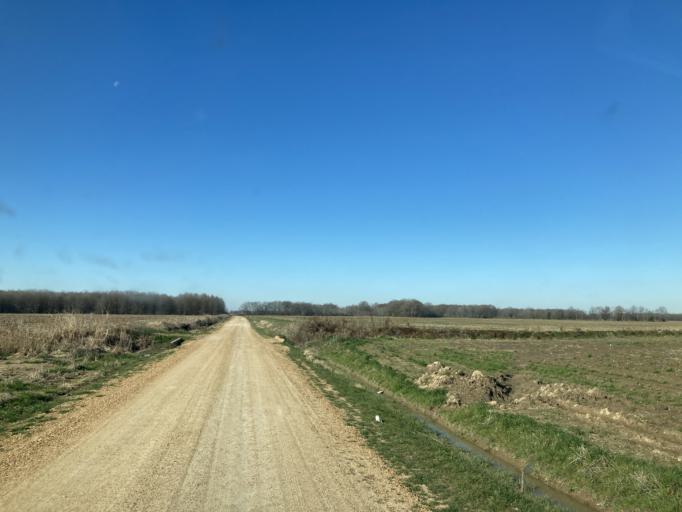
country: US
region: Mississippi
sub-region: Yazoo County
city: Yazoo City
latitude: 32.9519
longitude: -90.6063
